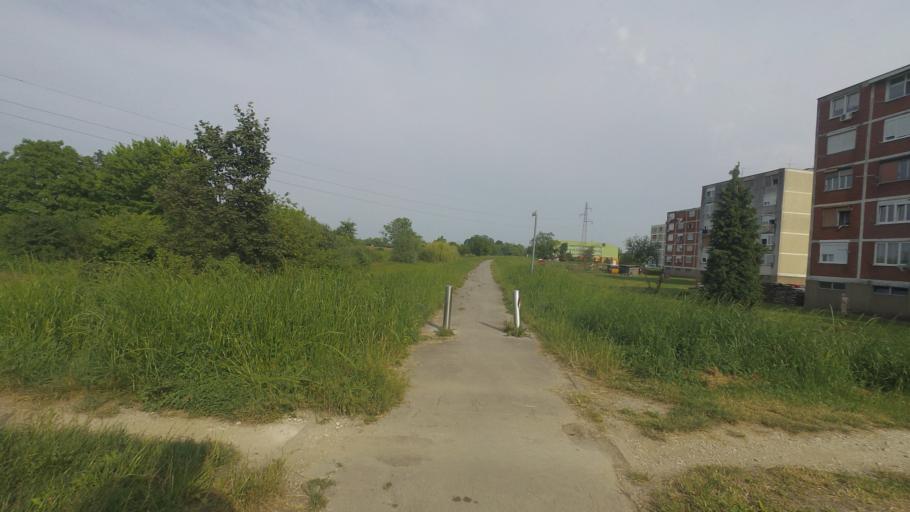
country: HR
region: Karlovacka
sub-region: Grad Karlovac
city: Karlovac
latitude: 45.5033
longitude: 15.5603
